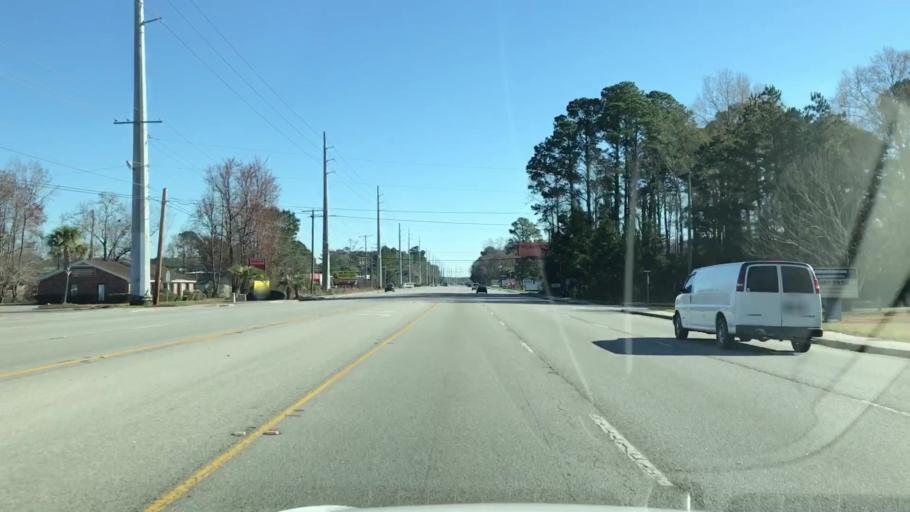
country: US
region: South Carolina
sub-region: Berkeley County
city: Ladson
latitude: 32.9218
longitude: -80.0970
